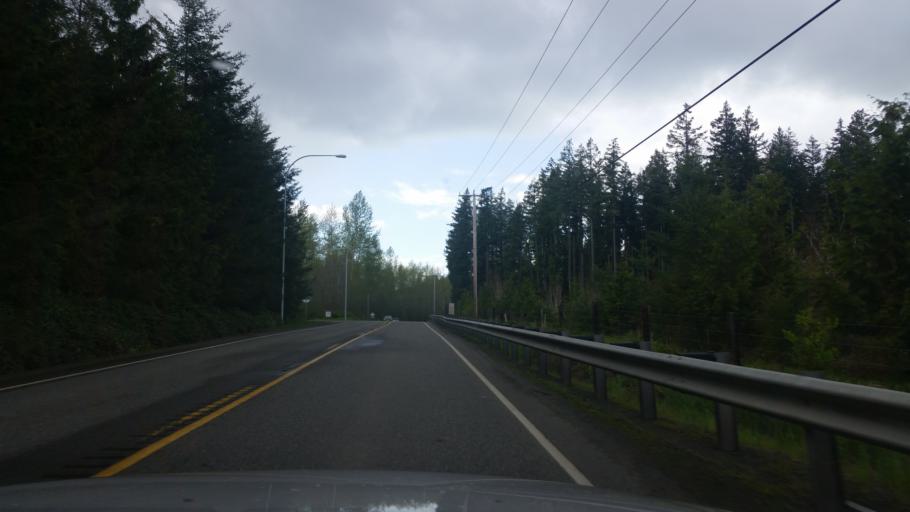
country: US
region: Washington
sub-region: Pierce County
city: Eatonville
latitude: 46.9496
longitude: -122.2936
